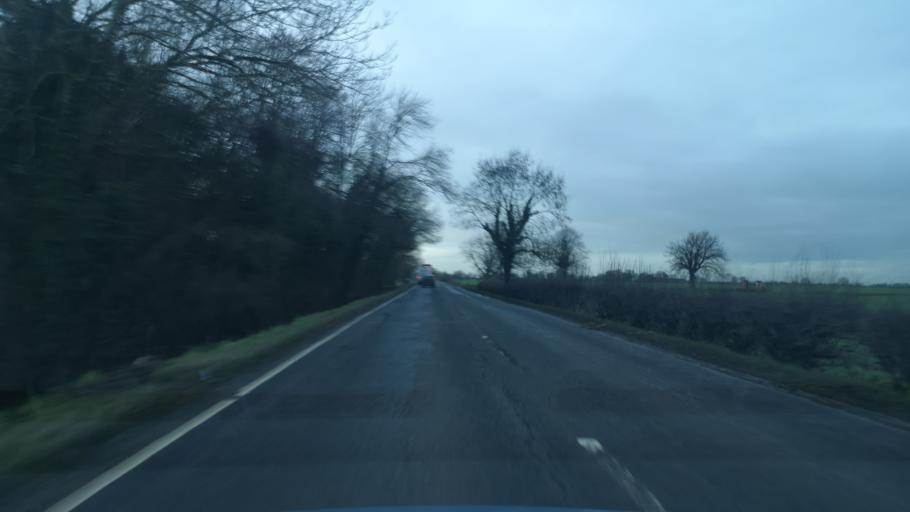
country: GB
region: England
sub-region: North Lincolnshire
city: Crowle
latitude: 53.5842
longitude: -0.9022
